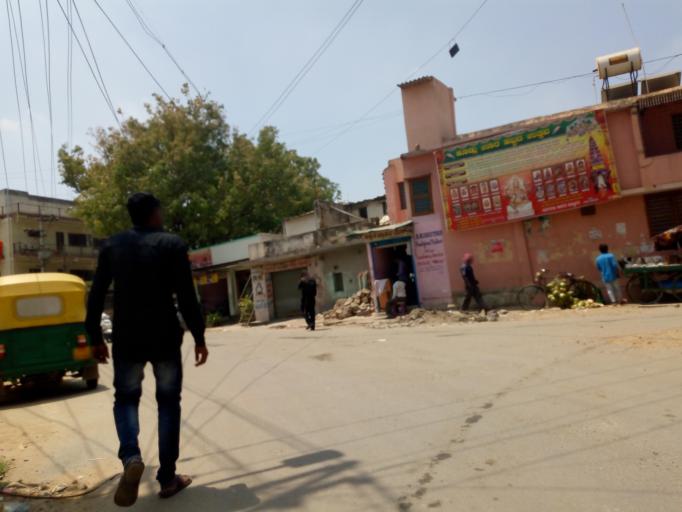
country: IN
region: Karnataka
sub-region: Bangalore Urban
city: Bangalore
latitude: 12.8898
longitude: 77.6564
